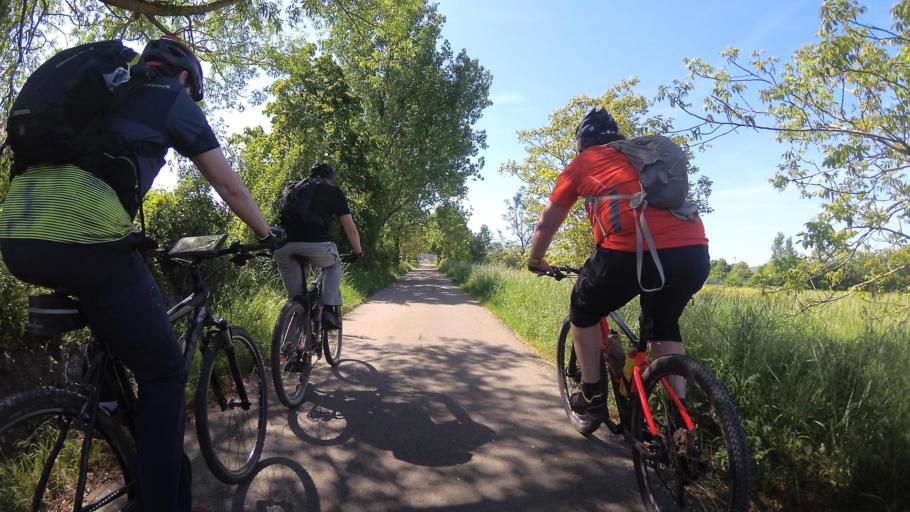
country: DE
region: Saarland
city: Gersheim
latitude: 49.1993
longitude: 7.1864
